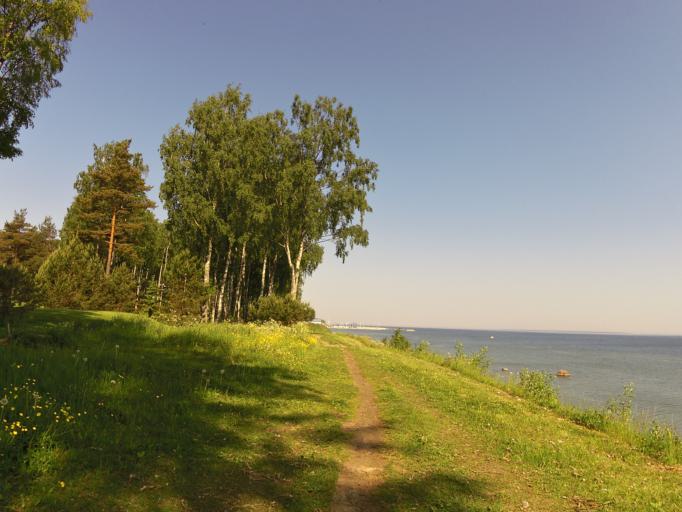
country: EE
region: Harju
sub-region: Harku vald
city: Tabasalu
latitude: 59.4443
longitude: 24.6208
